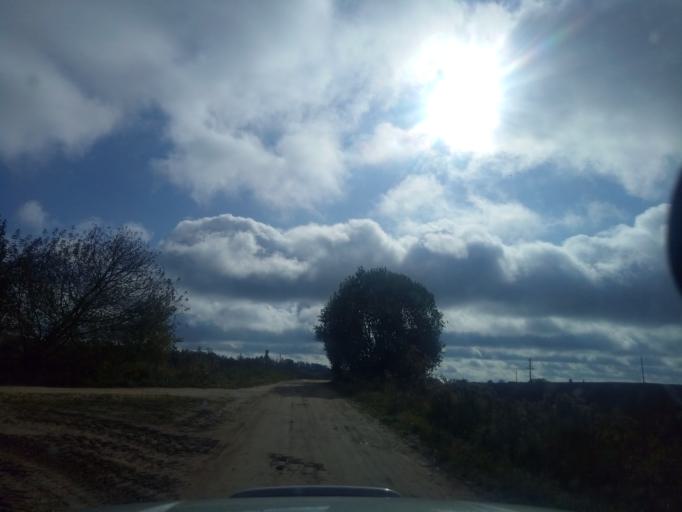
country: BY
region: Minsk
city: Zaslawye
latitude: 54.0214
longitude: 27.2889
